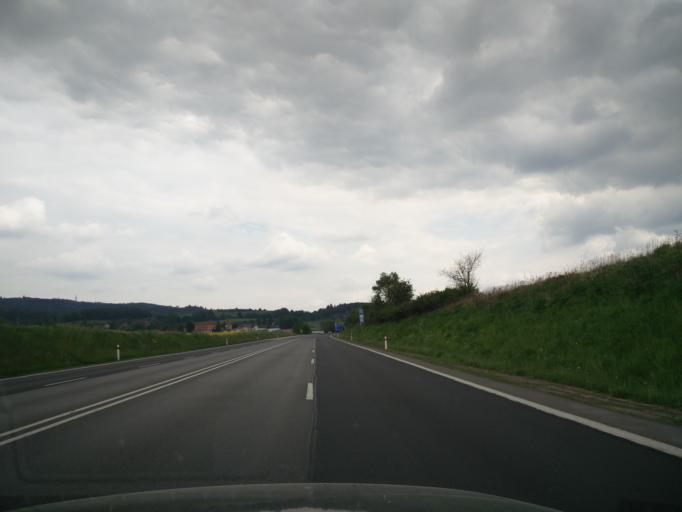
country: CZ
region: Jihocesky
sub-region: Okres Pisek
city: Pisek
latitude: 49.2961
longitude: 14.1525
